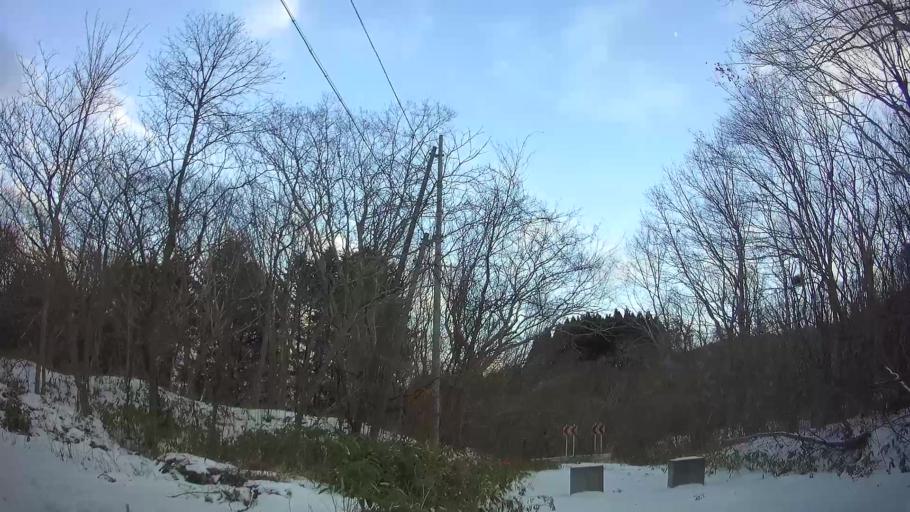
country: JP
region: Hokkaido
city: Nanae
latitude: 42.0189
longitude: 140.8432
